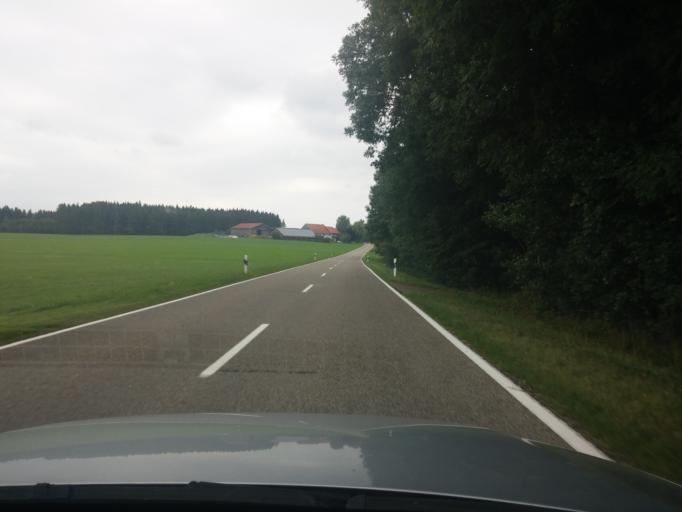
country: DE
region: Bavaria
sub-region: Swabia
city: Kronburg
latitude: 47.9169
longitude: 10.1504
